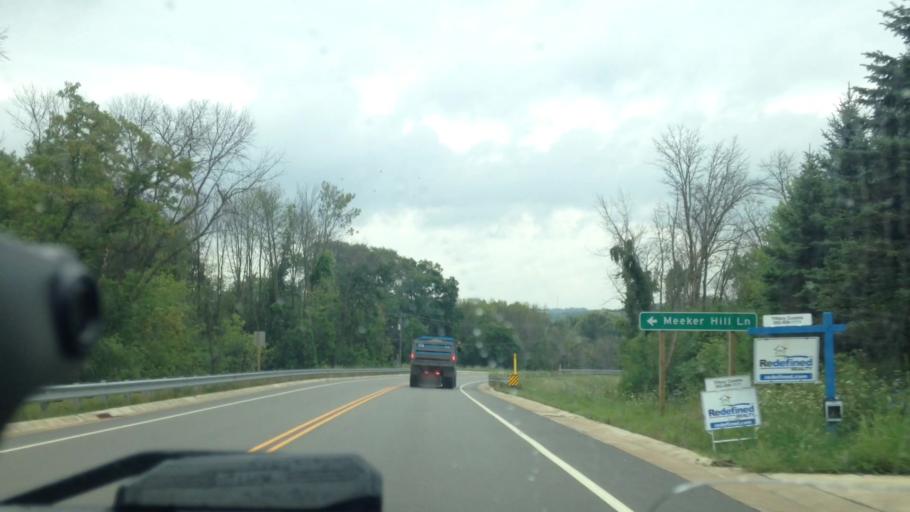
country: US
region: Wisconsin
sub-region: Washington County
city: Richfield
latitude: 43.2210
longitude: -88.1736
